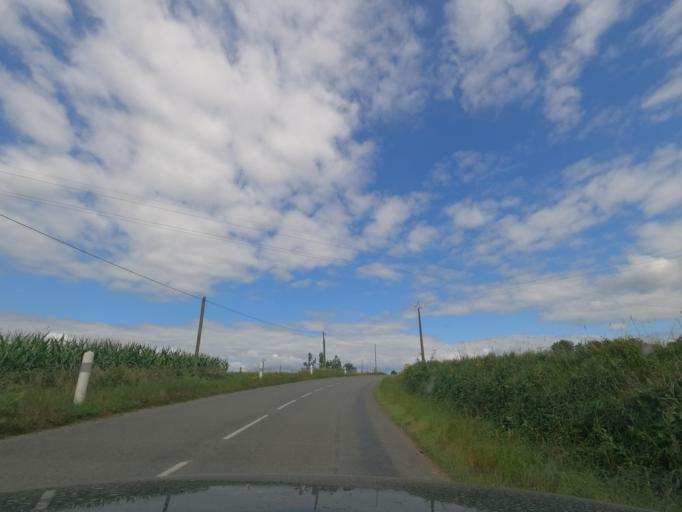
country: FR
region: Pays de la Loire
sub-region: Departement de la Mayenne
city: Landivy
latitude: 48.4566
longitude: -1.0623
